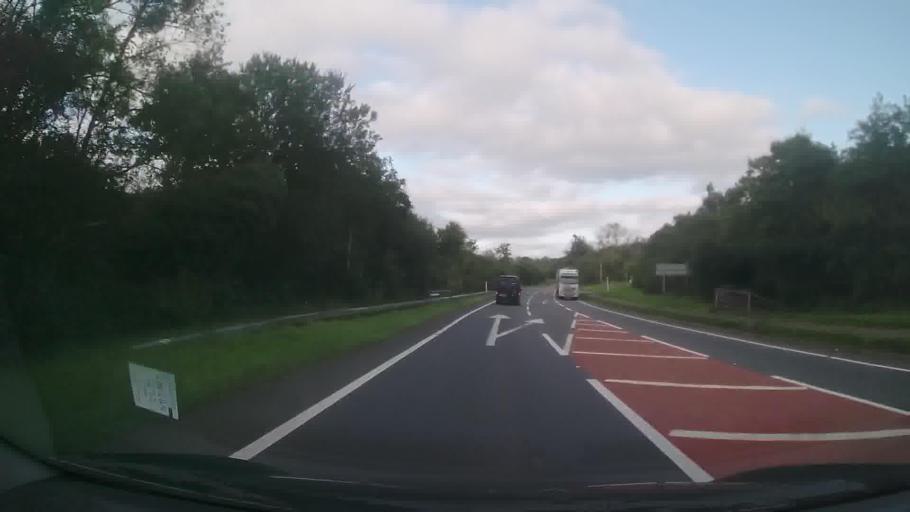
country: GB
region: Wales
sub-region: Pembrokeshire
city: Jeffreyston
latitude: 51.7061
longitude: -4.7694
